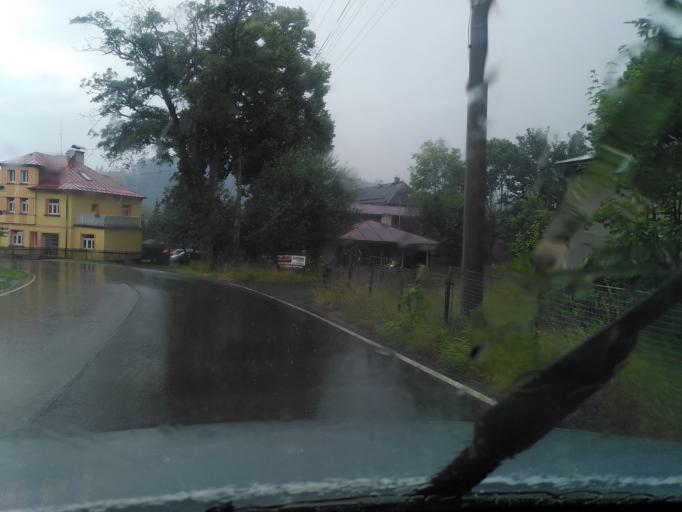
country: CZ
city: Novy Bor
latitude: 50.8116
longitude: 14.5368
